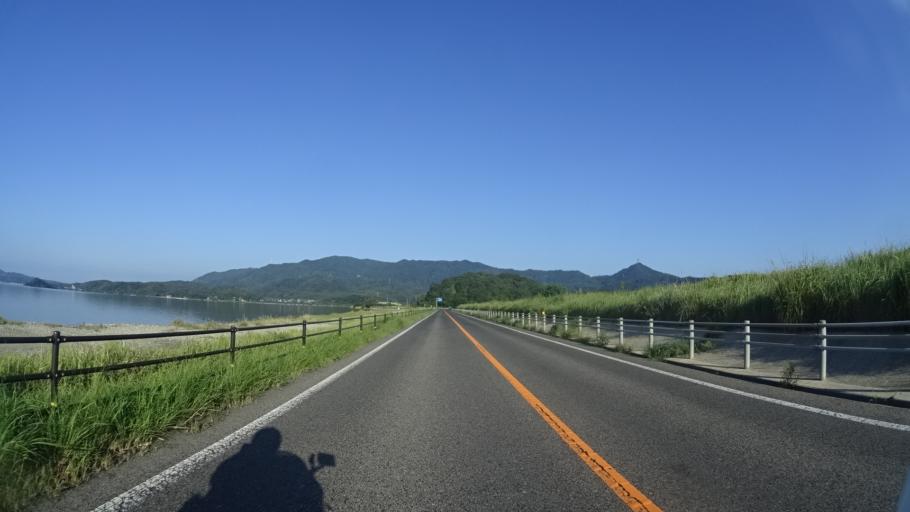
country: JP
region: Shimane
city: Sakaiminato
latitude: 35.5294
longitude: 133.1677
